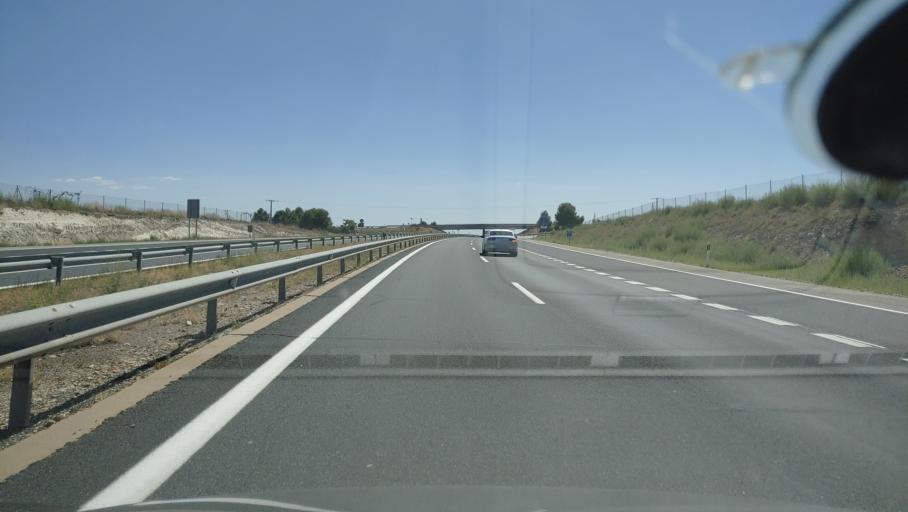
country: ES
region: Castille-La Mancha
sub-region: Provincia de Ciudad Real
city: Villarta de San Juan
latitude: 39.2390
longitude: -3.4125
